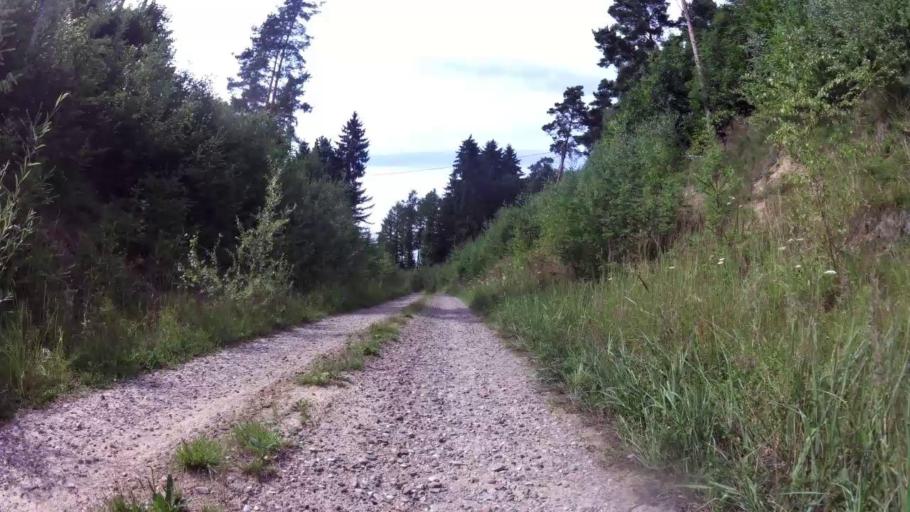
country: PL
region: West Pomeranian Voivodeship
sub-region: Powiat lobeski
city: Wegorzyno
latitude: 53.5246
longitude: 15.6447
